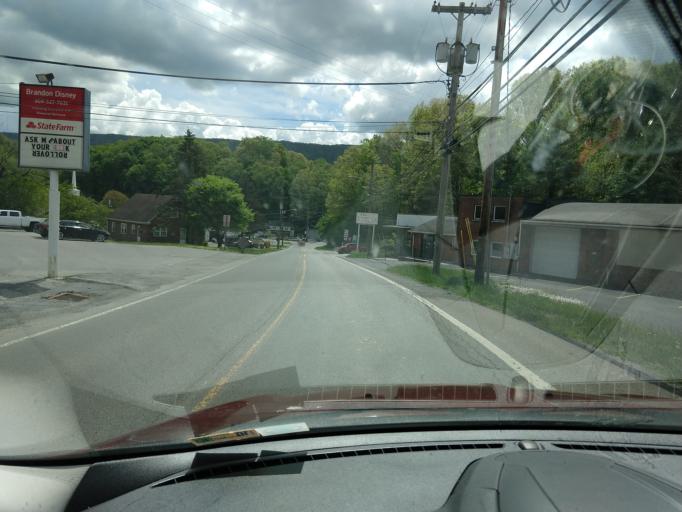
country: US
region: West Virginia
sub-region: Mercer County
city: Bluefield
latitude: 37.2547
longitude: -81.2337
